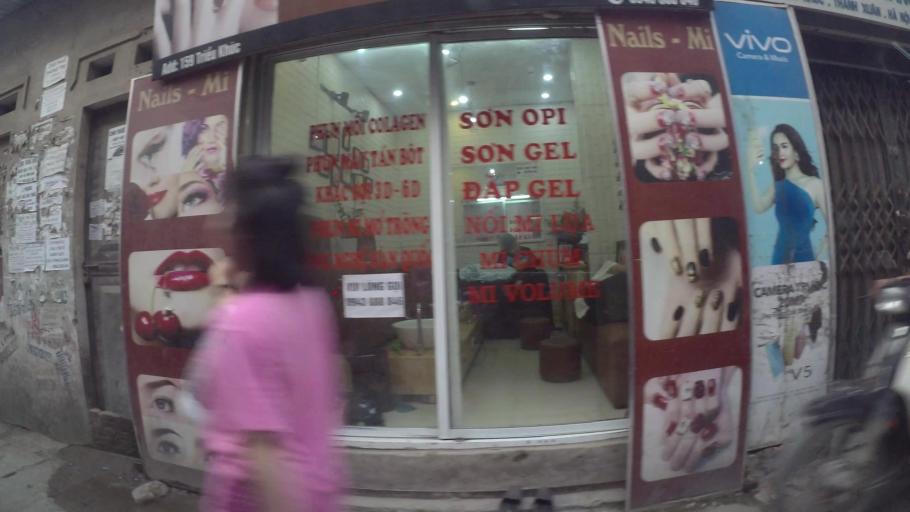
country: VN
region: Ha Noi
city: Thanh Xuan
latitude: 20.9821
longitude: 105.8007
